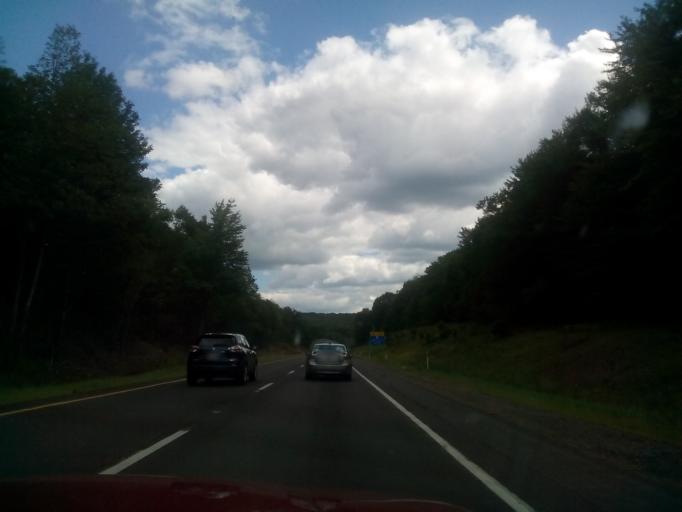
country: US
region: Pennsylvania
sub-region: Luzerne County
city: White Haven
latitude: 41.0577
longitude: -75.7336
